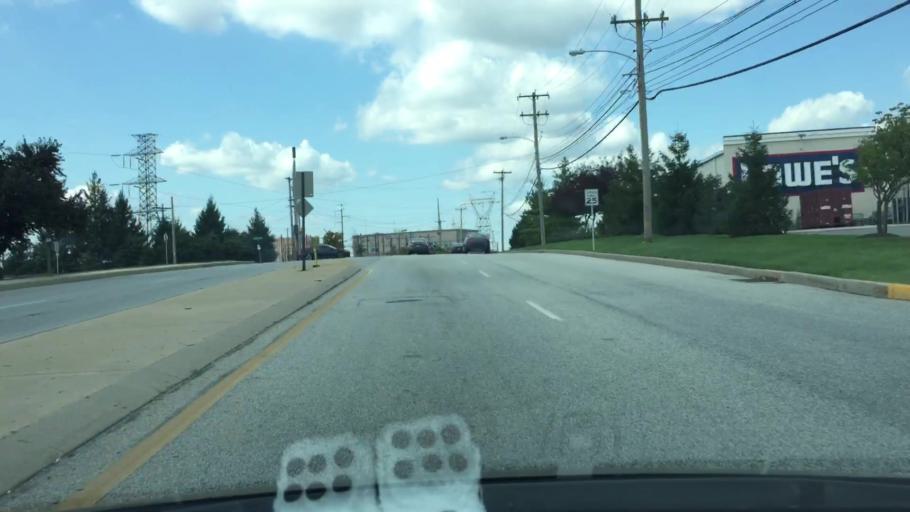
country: US
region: Pennsylvania
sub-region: Montgomery County
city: Plymouth Meeting
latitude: 40.1008
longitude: -75.2944
